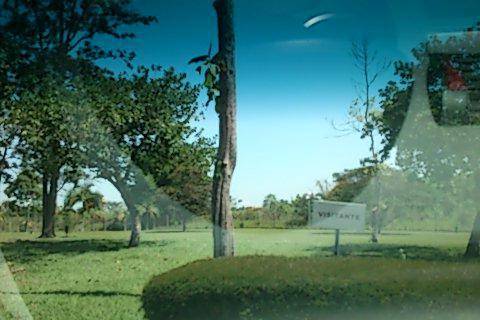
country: BR
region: Sao Paulo
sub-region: Sao Jose Dos Campos
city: Sao Jose dos Campos
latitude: -23.2065
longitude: -45.8612
